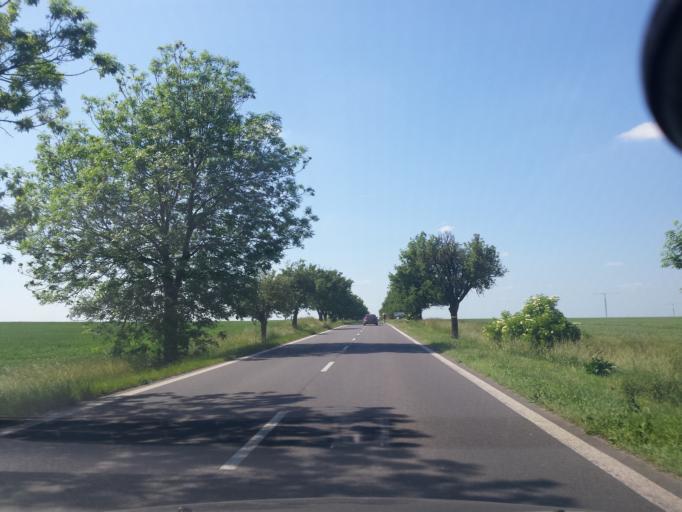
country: CZ
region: Central Bohemia
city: Horomerice
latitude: 50.1239
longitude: 14.3512
